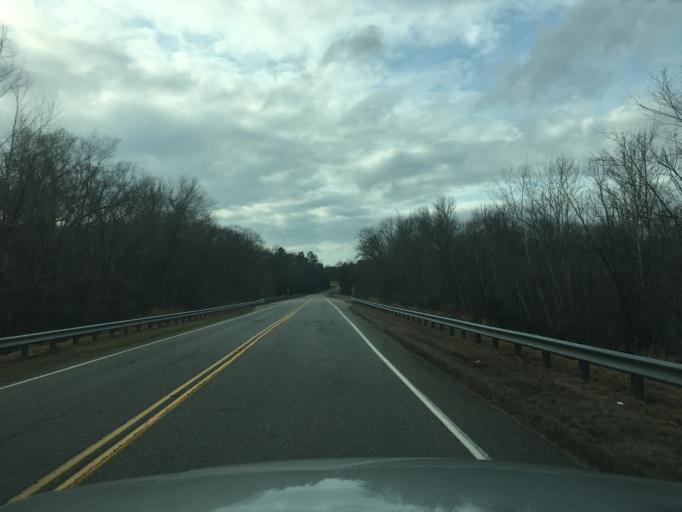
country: US
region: South Carolina
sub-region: Abbeville County
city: Due West
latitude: 34.2871
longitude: -82.4402
